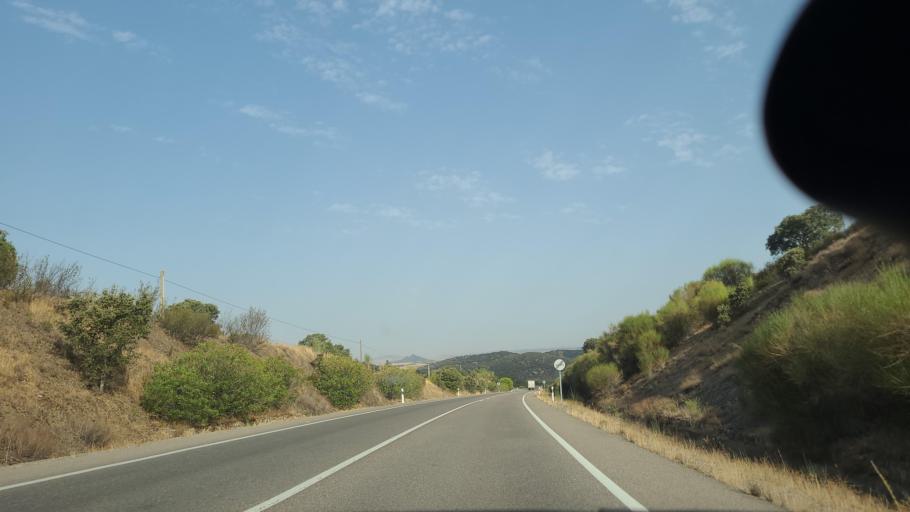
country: ES
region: Andalusia
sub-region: Province of Cordoba
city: Espiel
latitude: 38.1934
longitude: -5.0975
